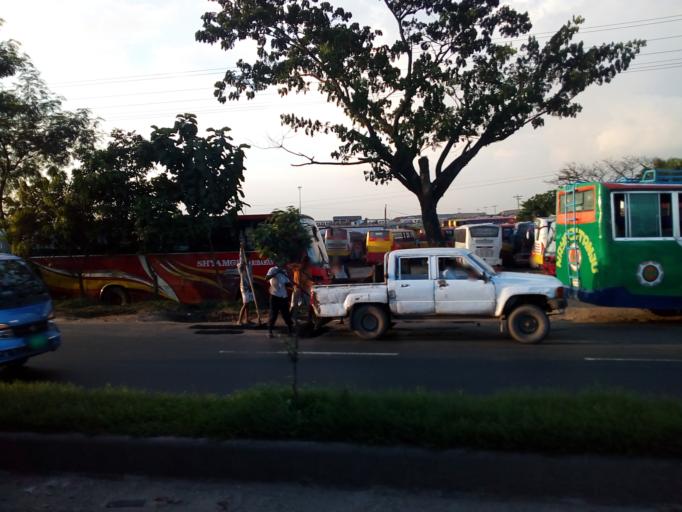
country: BD
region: Dhaka
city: Azimpur
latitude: 23.7932
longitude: 90.2989
